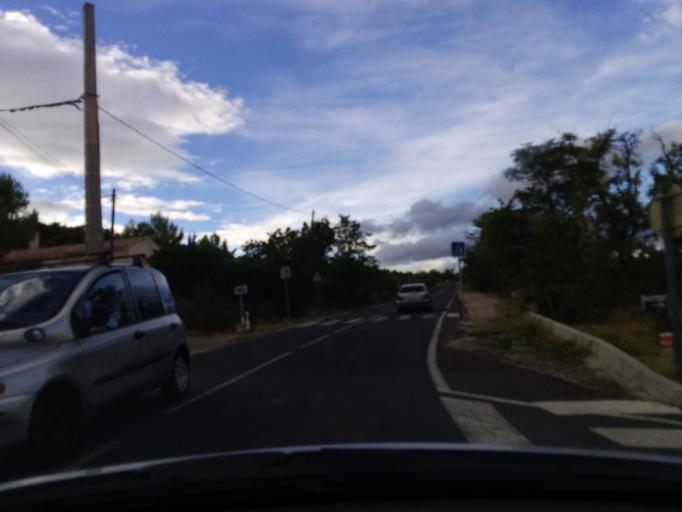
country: FR
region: Languedoc-Roussillon
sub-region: Departement de l'Herault
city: Nebian
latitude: 43.6360
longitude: 3.4182
